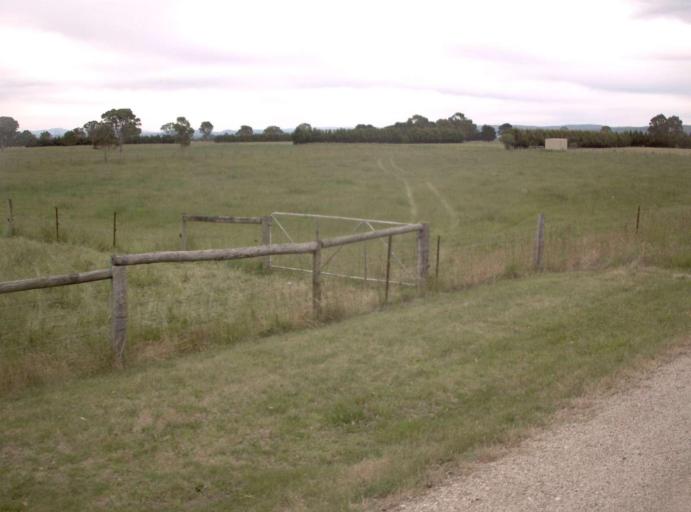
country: AU
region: Victoria
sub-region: East Gippsland
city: Bairnsdale
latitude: -37.8697
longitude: 147.5614
